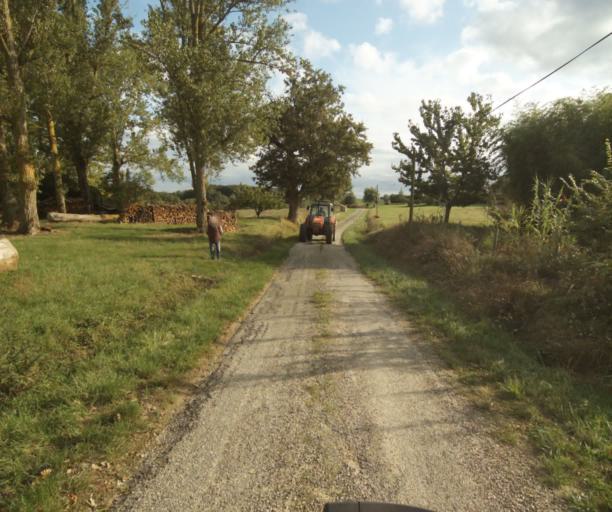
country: FR
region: Midi-Pyrenees
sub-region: Departement du Tarn-et-Garonne
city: Verdun-sur-Garonne
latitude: 43.8406
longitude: 1.1467
